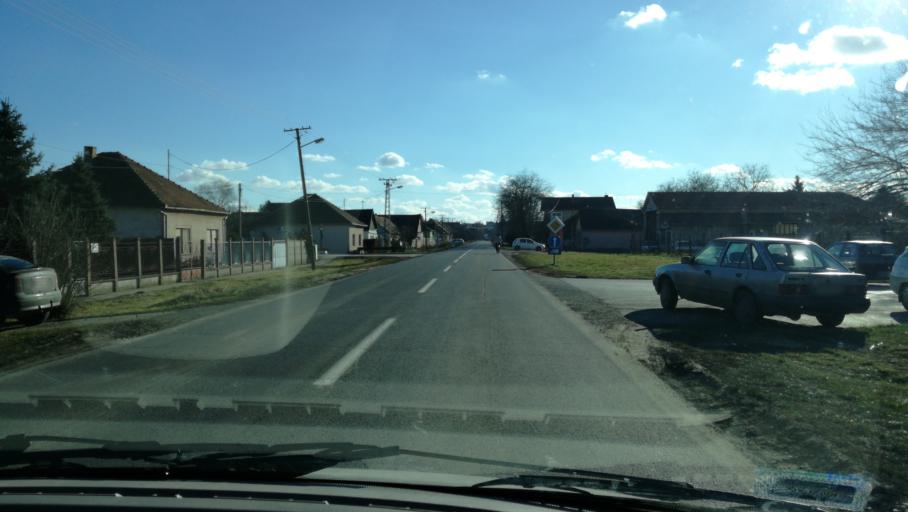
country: RS
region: Autonomna Pokrajina Vojvodina
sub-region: Severnobanatski Okrug
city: Coka
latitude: 45.9449
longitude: 20.1412
